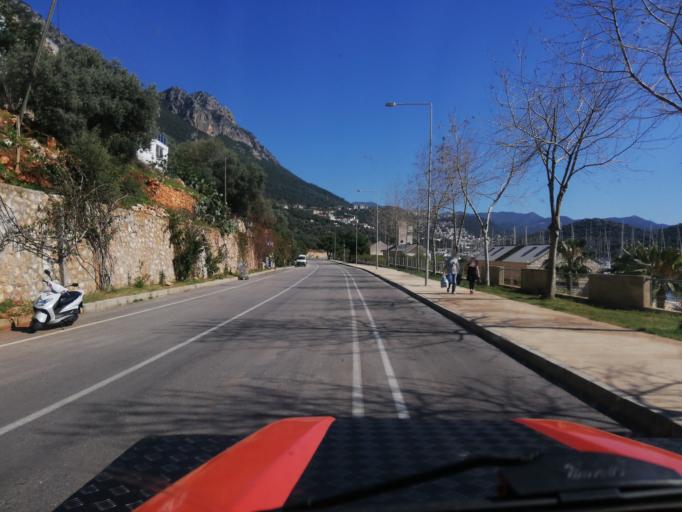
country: TR
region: Antalya
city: Kas
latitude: 36.2066
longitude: 29.6272
